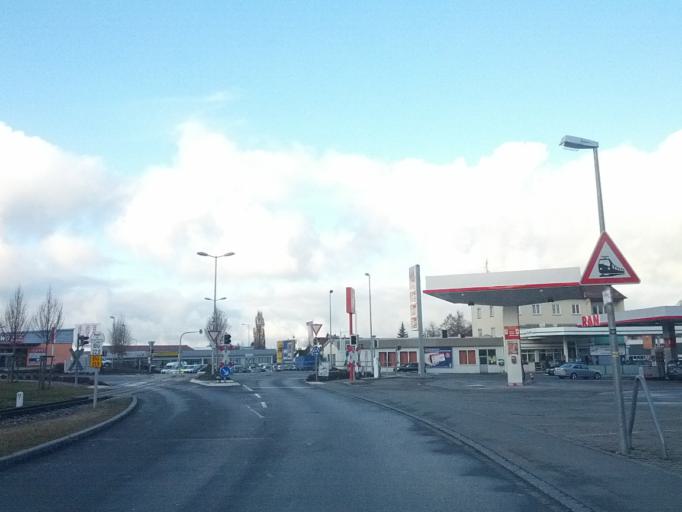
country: DE
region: Baden-Wuerttemberg
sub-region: Tuebingen Region
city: Ochsenhausen
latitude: 48.0720
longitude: 9.9479
